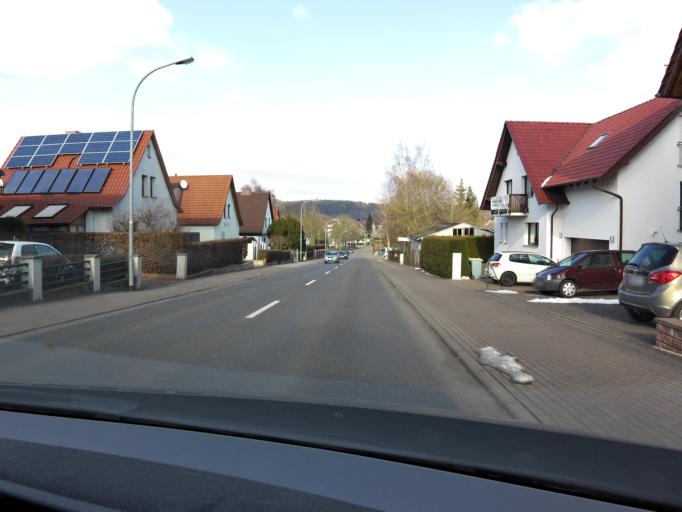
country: DE
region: Thuringia
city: Bad Salzungen
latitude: 50.8067
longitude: 10.2255
